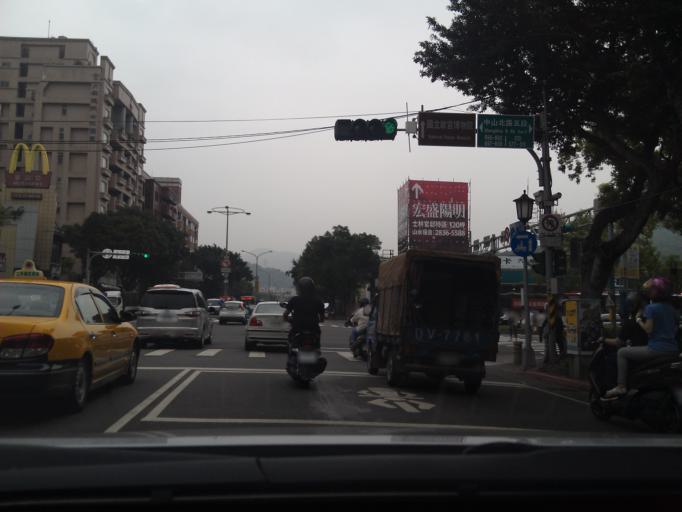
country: TW
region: Taipei
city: Taipei
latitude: 25.0956
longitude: 121.5274
